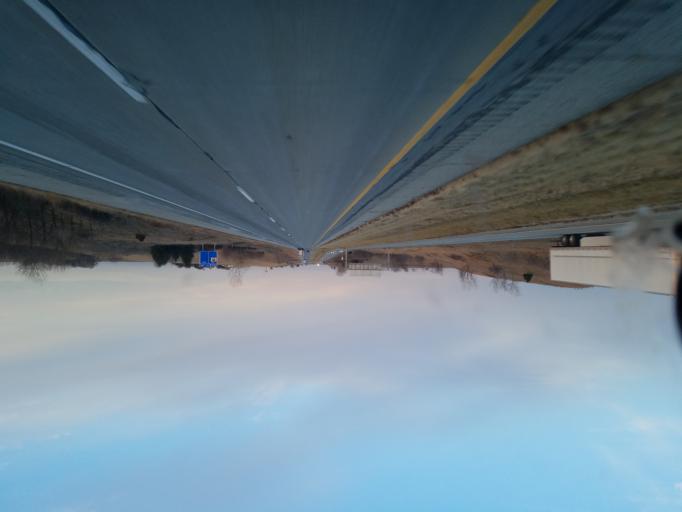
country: US
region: Iowa
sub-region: Pottawattamie County
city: Avoca
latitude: 41.4985
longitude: -95.5648
